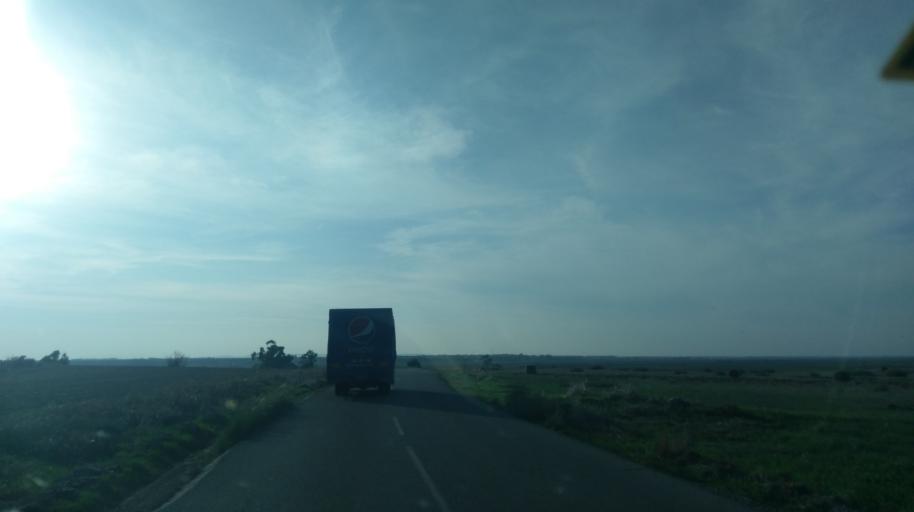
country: CY
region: Ammochostos
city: Acheritou
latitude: 35.0951
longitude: 33.8399
